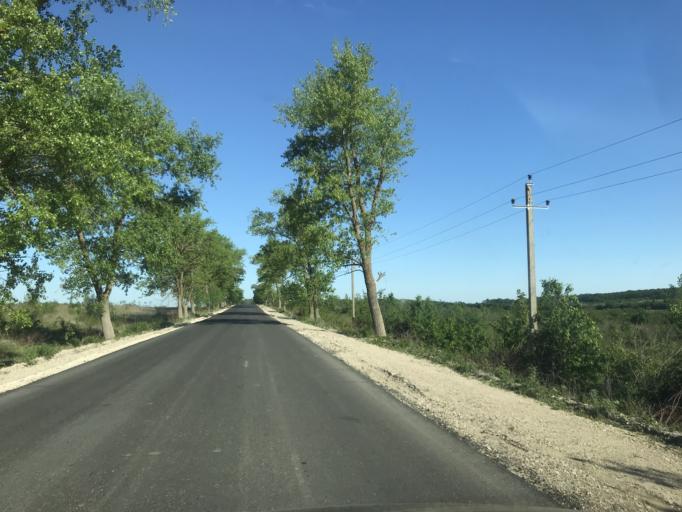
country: MD
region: Chisinau
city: Cricova
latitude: 47.2511
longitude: 28.8134
